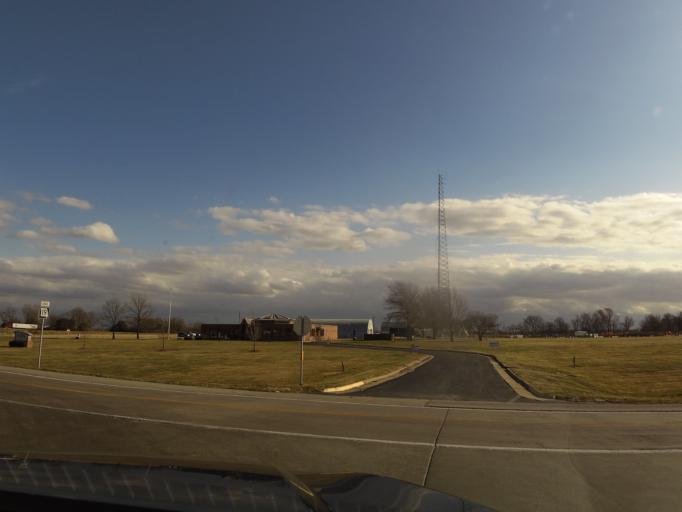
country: US
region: Missouri
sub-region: Ralls County
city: New London
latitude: 39.5730
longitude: -91.4035
